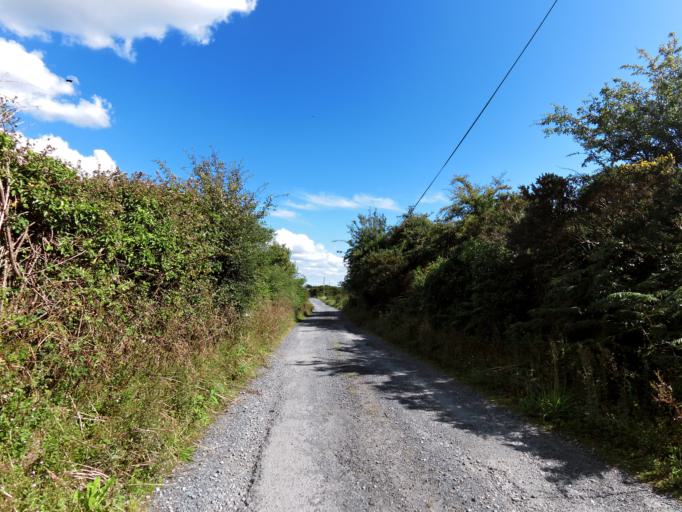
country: IE
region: Connaught
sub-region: County Galway
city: Gaillimh
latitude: 53.2852
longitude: -9.0894
